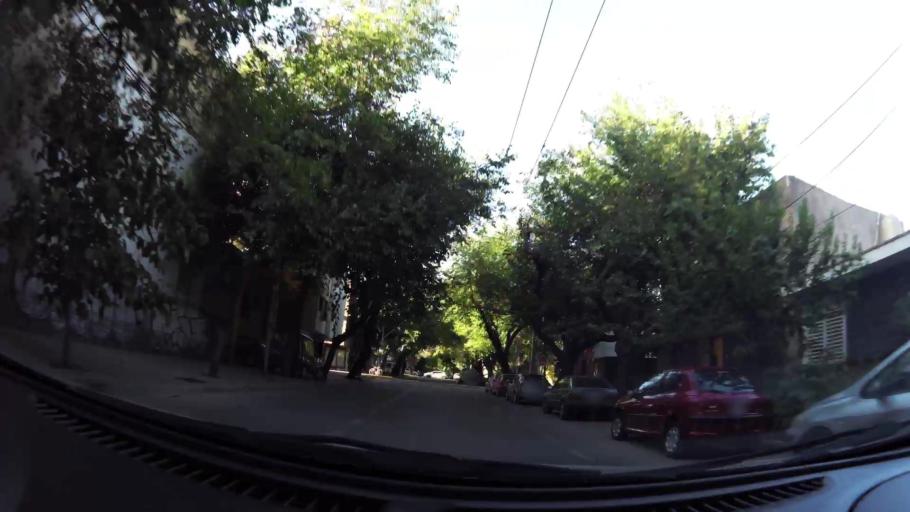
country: AR
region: Mendoza
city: Mendoza
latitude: -32.9003
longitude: -68.8433
